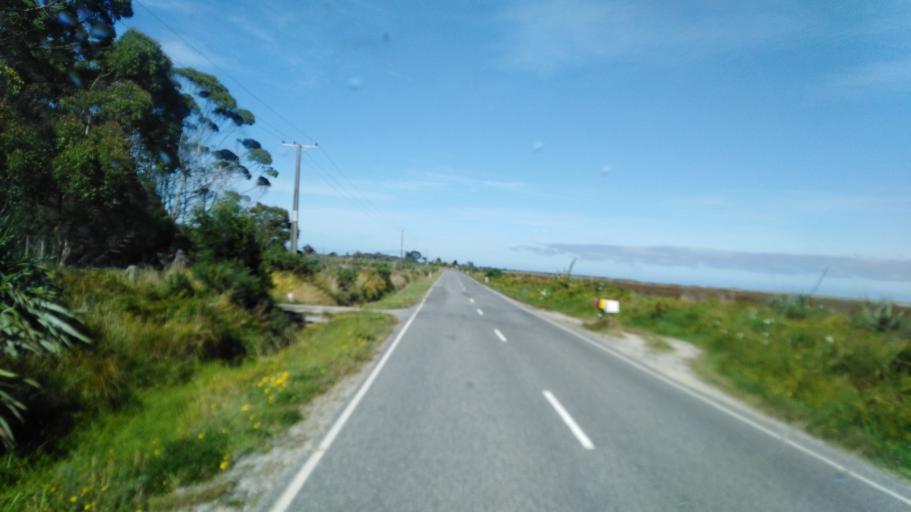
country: NZ
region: West Coast
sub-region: Buller District
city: Westport
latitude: -41.2812
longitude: 172.1071
